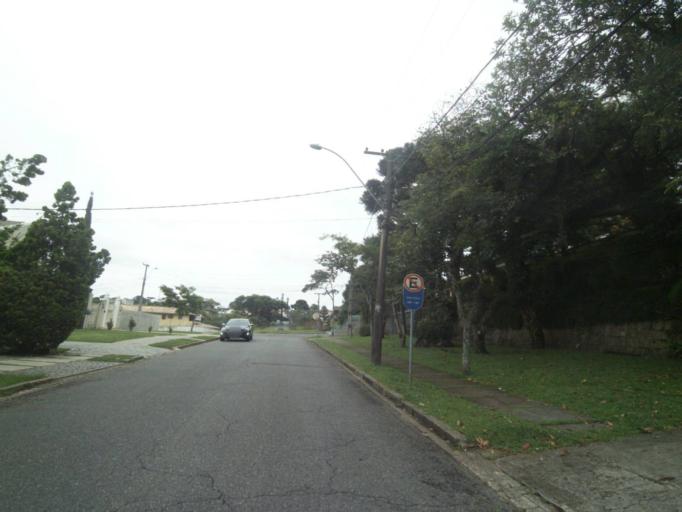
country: BR
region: Parana
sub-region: Curitiba
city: Curitiba
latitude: -25.4071
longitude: -49.2837
